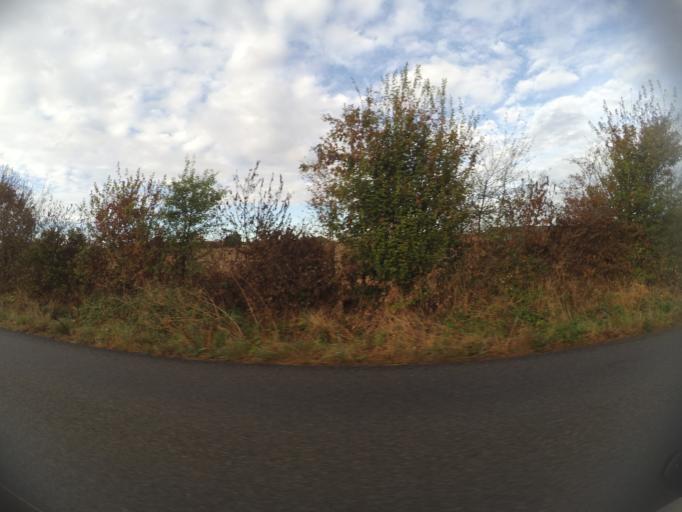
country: FR
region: Pays de la Loire
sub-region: Departement de la Loire-Atlantique
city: Saint-Lumine-de-Clisson
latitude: 47.0754
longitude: -1.3276
